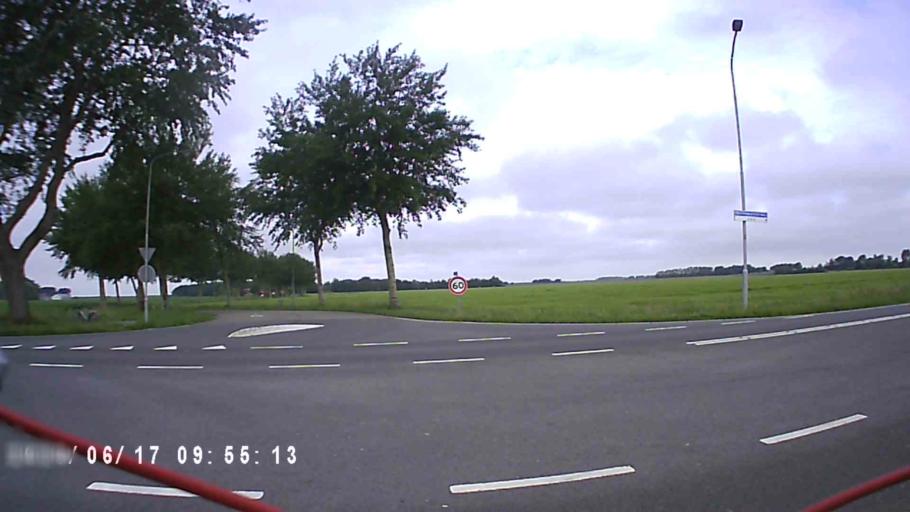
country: NL
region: Groningen
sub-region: Gemeente De Marne
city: Ulrum
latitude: 53.3595
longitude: 6.3062
